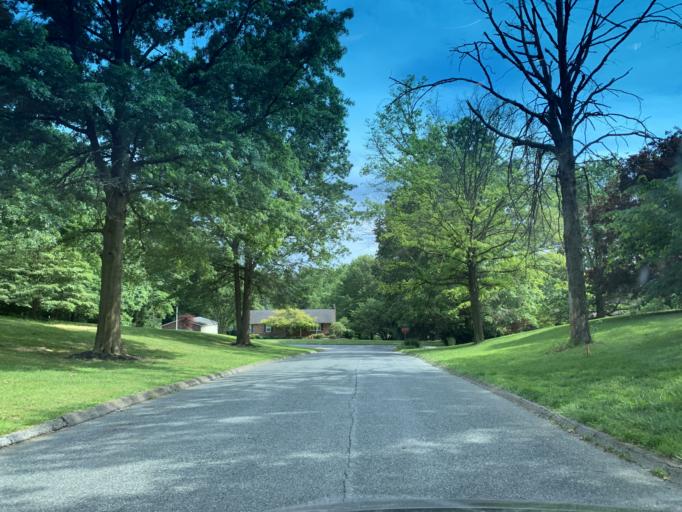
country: US
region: Maryland
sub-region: Harford County
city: Jarrettsville
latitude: 39.6033
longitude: -76.4624
